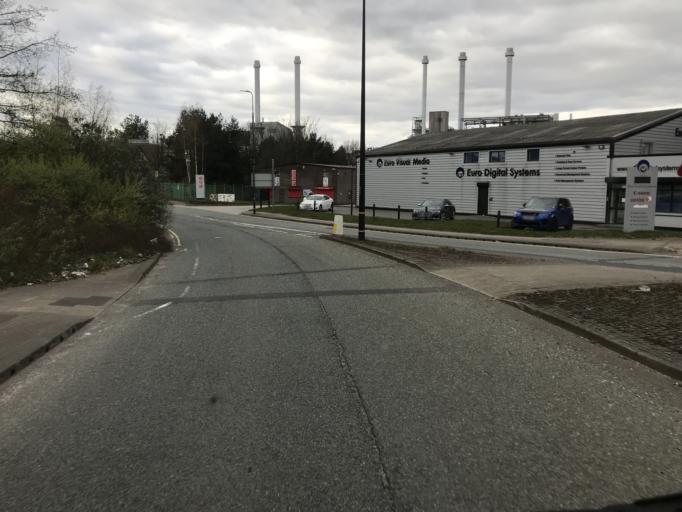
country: GB
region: England
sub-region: City and Borough of Salford
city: Eccles
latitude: 53.4760
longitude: -2.3268
